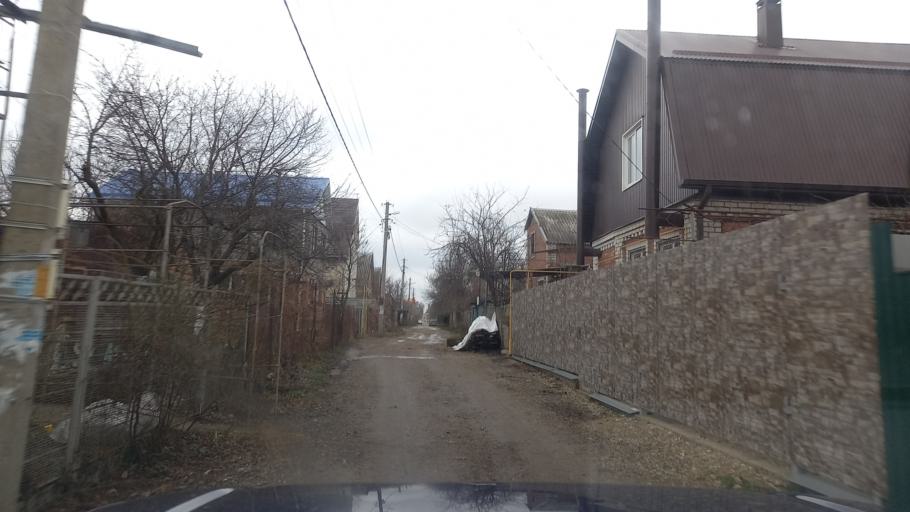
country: RU
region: Krasnodarskiy
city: Pashkovskiy
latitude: 45.0525
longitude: 39.1765
